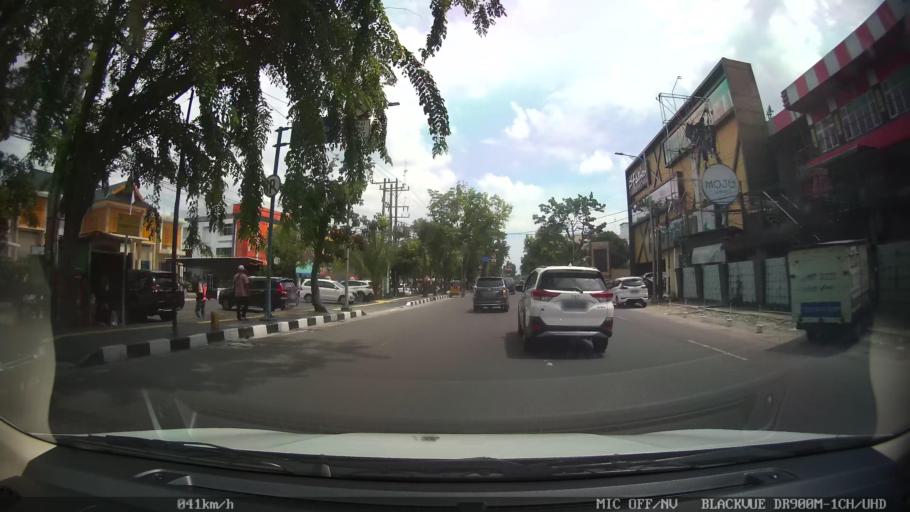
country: ID
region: North Sumatra
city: Medan
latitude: 3.5865
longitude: 98.6613
